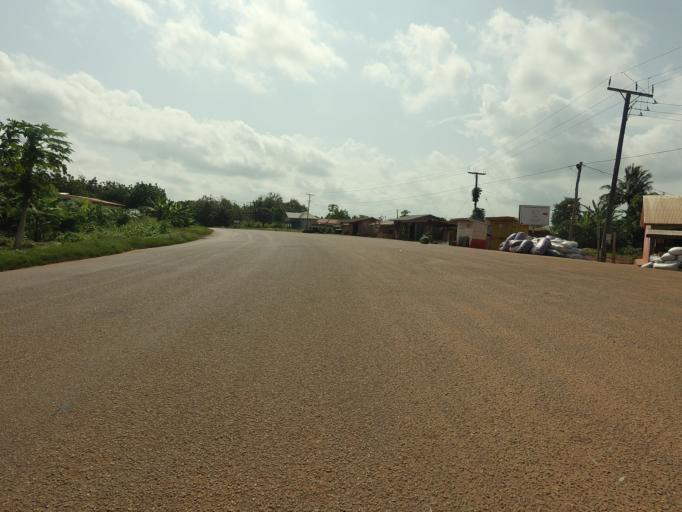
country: TG
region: Maritime
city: Tsevie
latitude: 6.3606
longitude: 0.8651
